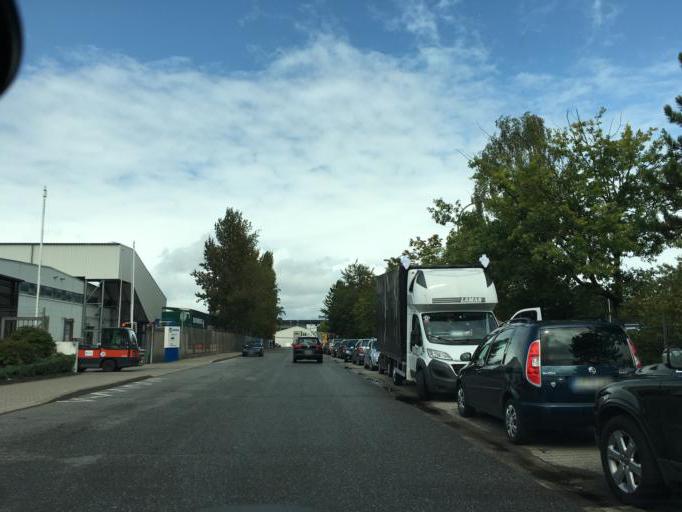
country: DE
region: Lower Saxony
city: Adendorf
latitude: 53.2759
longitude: 10.4226
